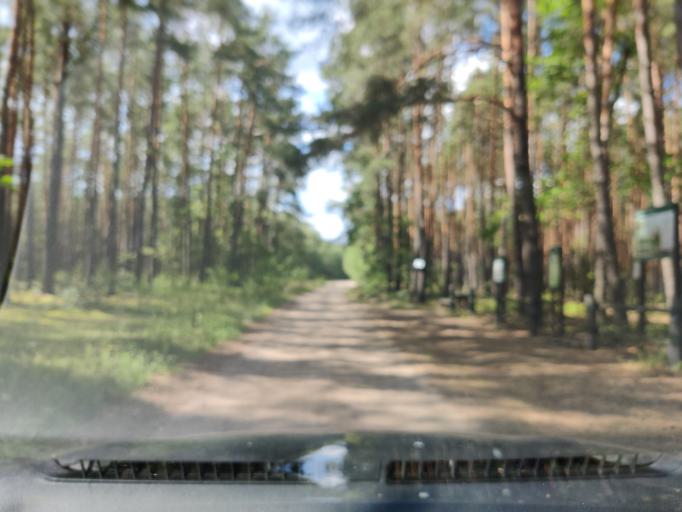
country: PL
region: Masovian Voivodeship
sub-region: Powiat pultuski
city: Pultusk
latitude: 52.7332
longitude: 21.1558
